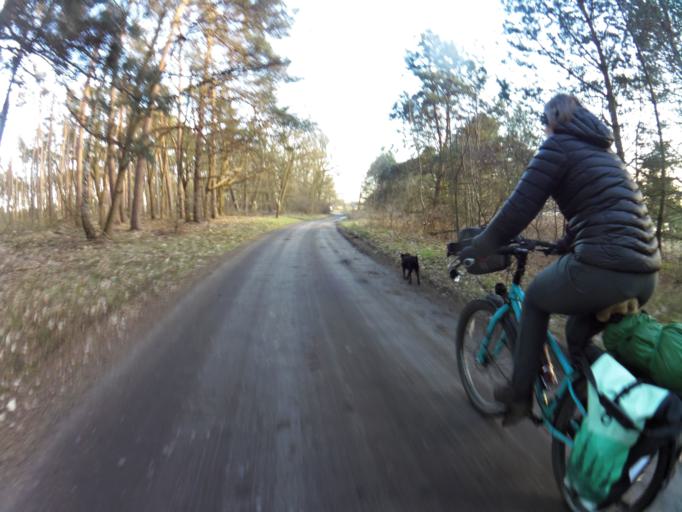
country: PL
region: West Pomeranian Voivodeship
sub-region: Powiat mysliborski
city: Debno
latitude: 52.8195
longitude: 14.7847
